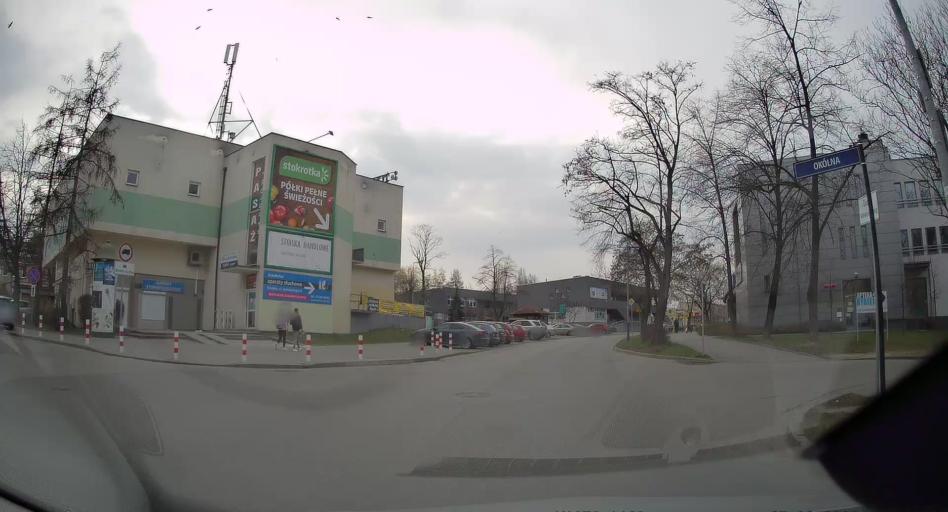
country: PL
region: Lesser Poland Voivodeship
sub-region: Krakow
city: Krakow
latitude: 50.0184
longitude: 19.9834
